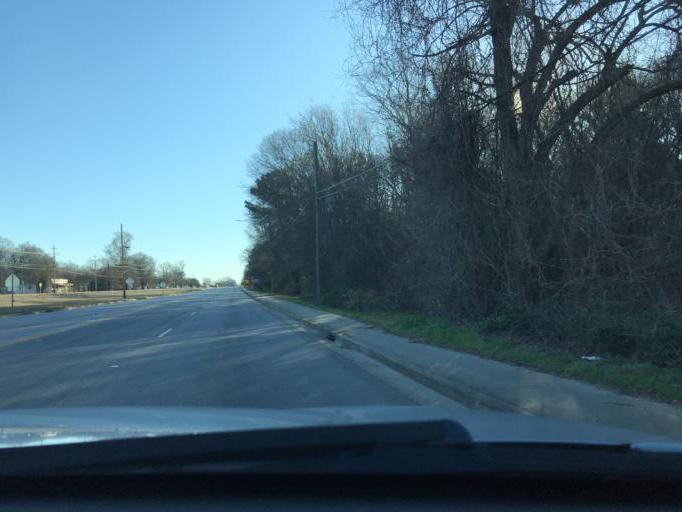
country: US
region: South Carolina
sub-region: Laurens County
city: Clinton
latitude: 34.4709
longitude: -81.8971
